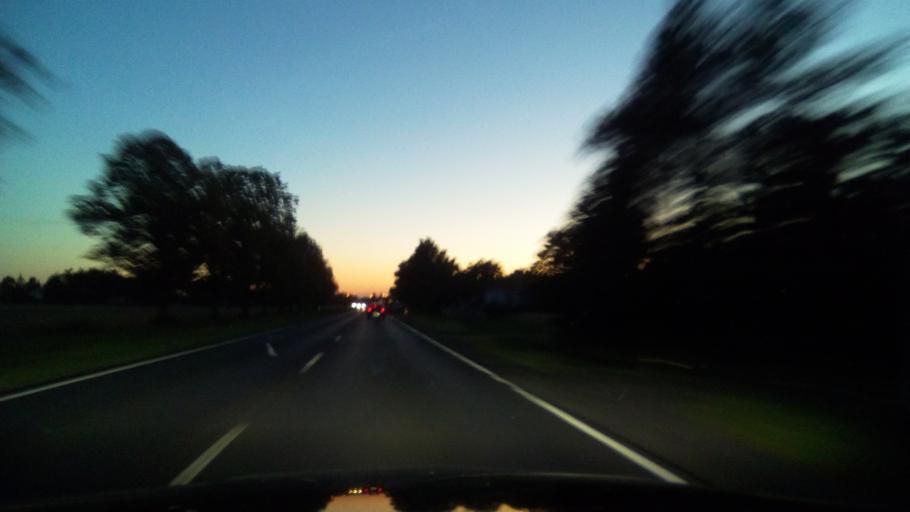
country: PL
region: Greater Poland Voivodeship
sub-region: Powiat koninski
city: Golina
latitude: 52.2479
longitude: 18.0245
